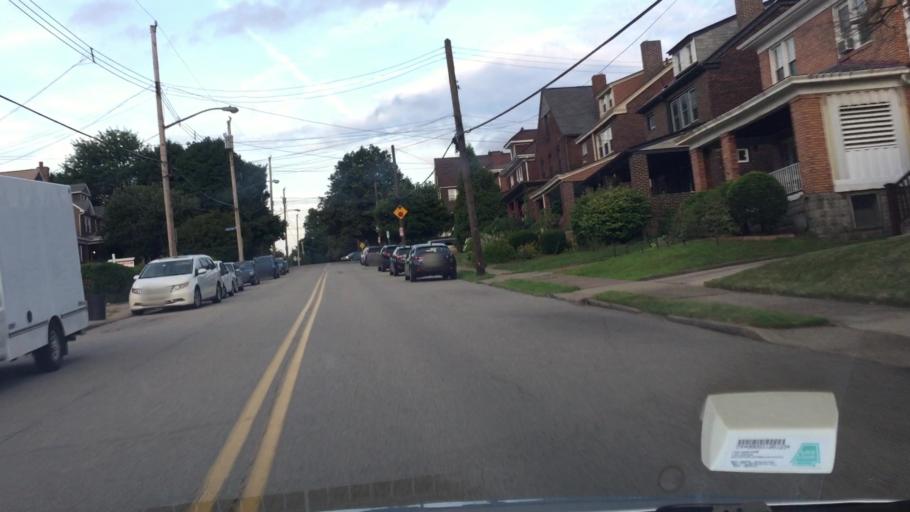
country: US
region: Pennsylvania
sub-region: Allegheny County
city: Homestead
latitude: 40.4252
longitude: -79.9217
